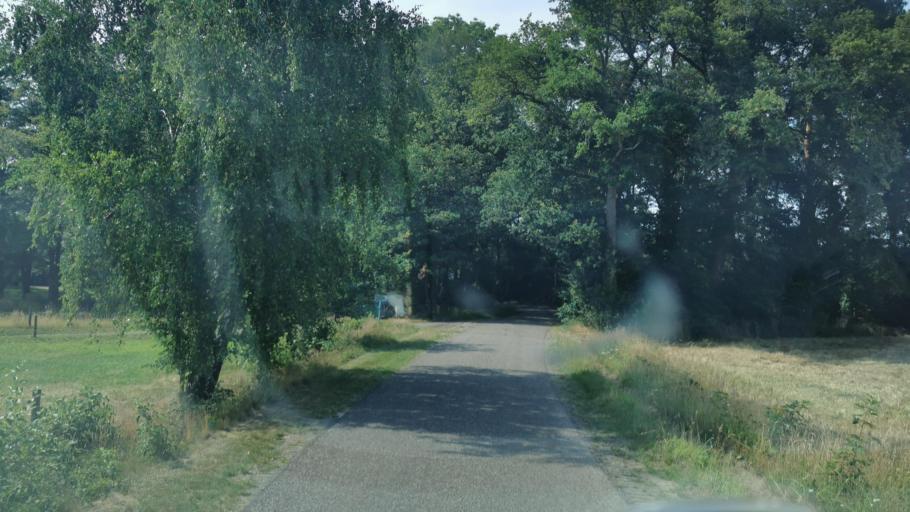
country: NL
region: Overijssel
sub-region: Gemeente Oldenzaal
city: Oldenzaal
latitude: 52.3069
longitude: 6.8639
